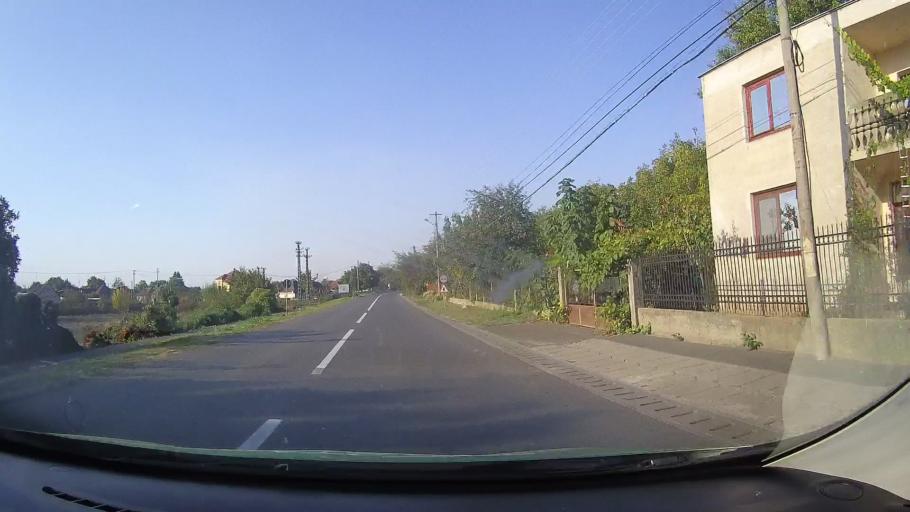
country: RO
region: Arad
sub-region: Comuna Ghioroc
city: Cuvin
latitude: 46.1606
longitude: 21.5922
